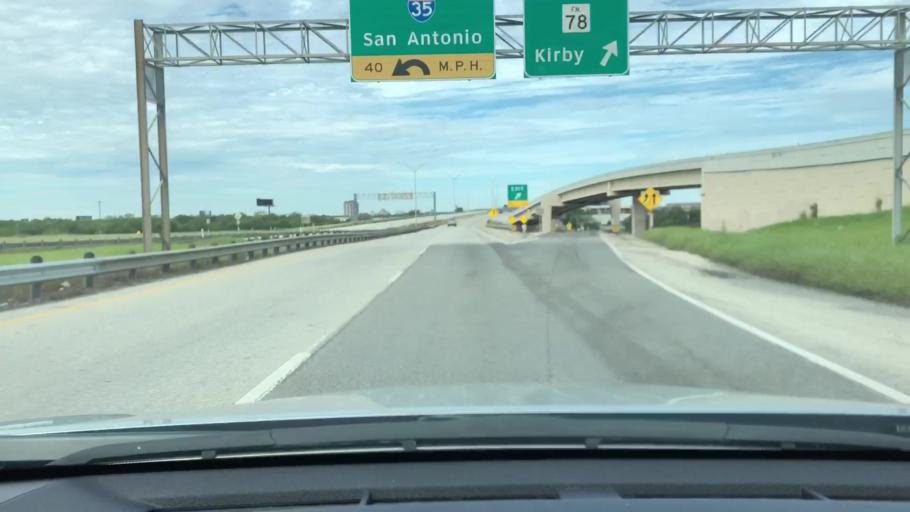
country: US
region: Texas
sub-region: Bexar County
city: Kirby
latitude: 29.4526
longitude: -98.4078
